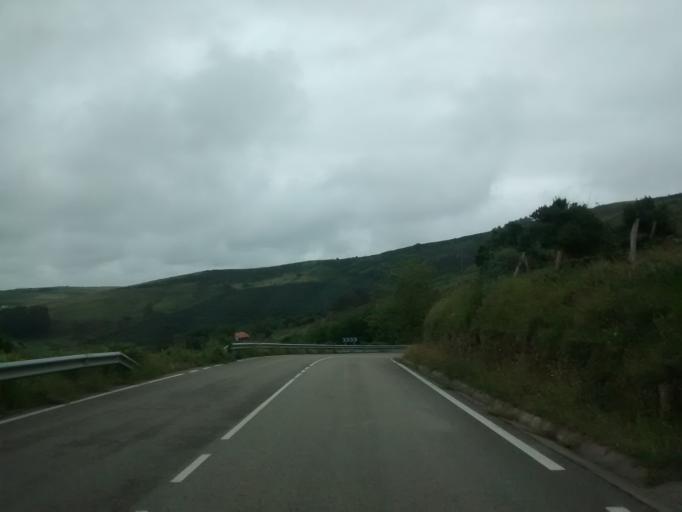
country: ES
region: Cantabria
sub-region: Provincia de Cantabria
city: Santillana
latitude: 43.4109
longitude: -4.1074
